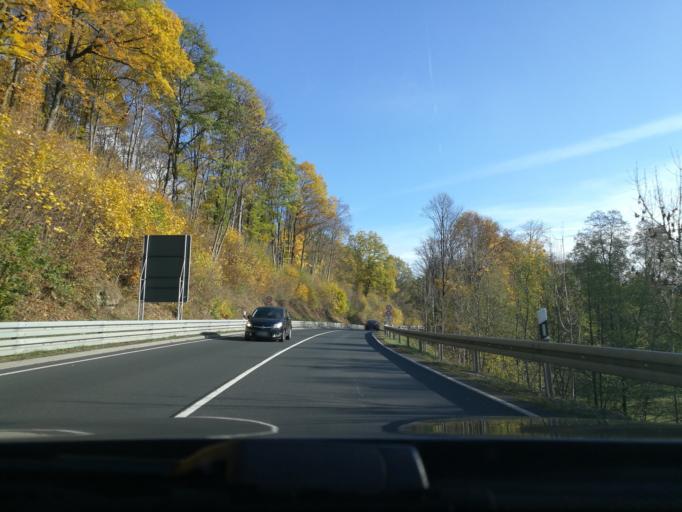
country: DE
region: Hesse
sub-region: Regierungsbezirk Kassel
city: Gersfeld
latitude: 50.4545
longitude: 9.8981
